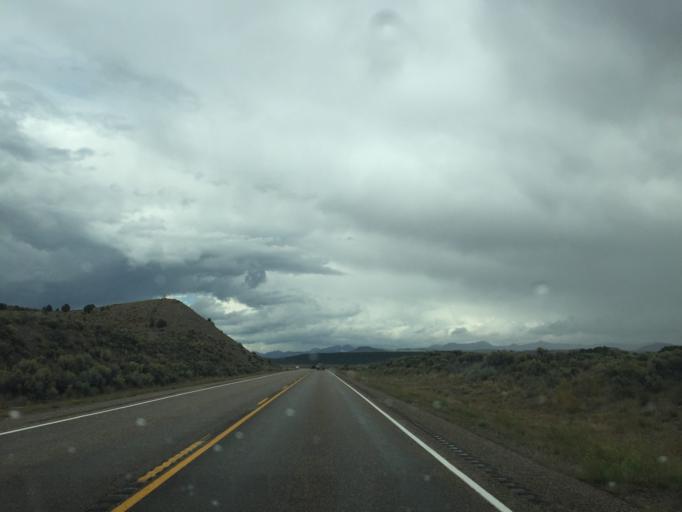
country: US
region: Utah
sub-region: Garfield County
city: Panguitch
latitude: 37.7280
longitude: -112.3817
